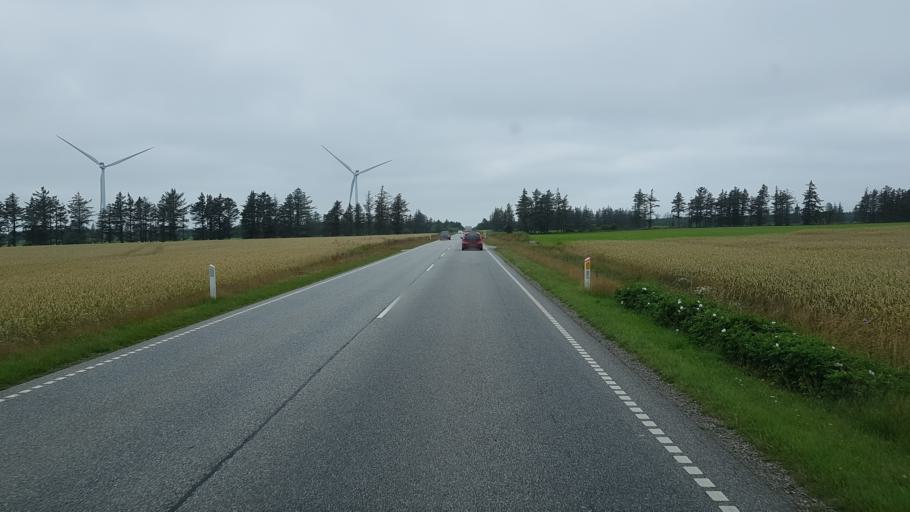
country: DK
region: Central Jutland
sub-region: Lemvig Kommune
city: Lemvig
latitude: 56.4441
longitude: 8.3602
